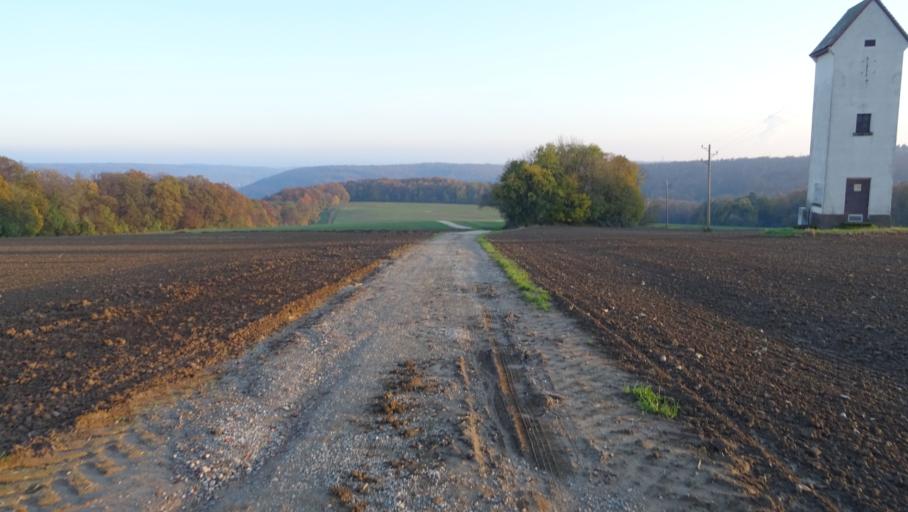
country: DE
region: Baden-Wuerttemberg
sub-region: Karlsruhe Region
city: Obrigheim
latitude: 49.3311
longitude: 9.0880
